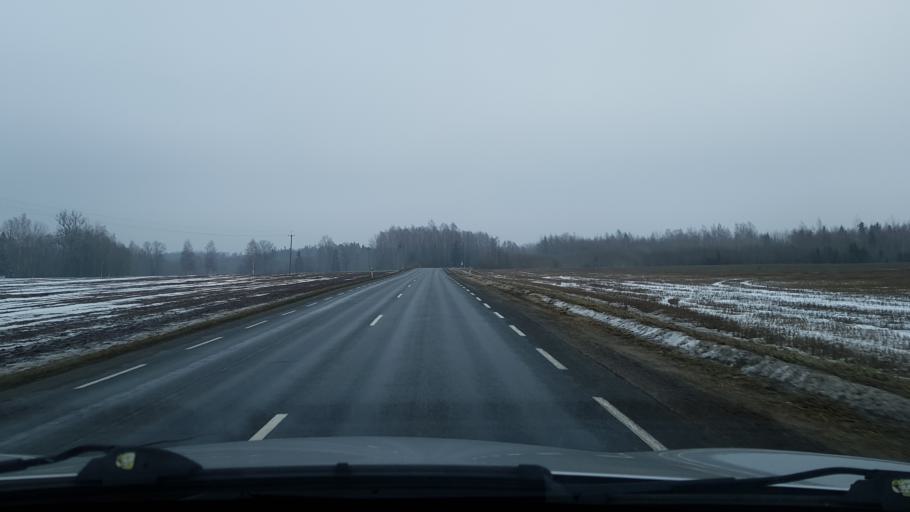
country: EE
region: Viljandimaa
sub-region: Viiratsi vald
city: Viiratsi
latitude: 58.2497
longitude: 25.7899
